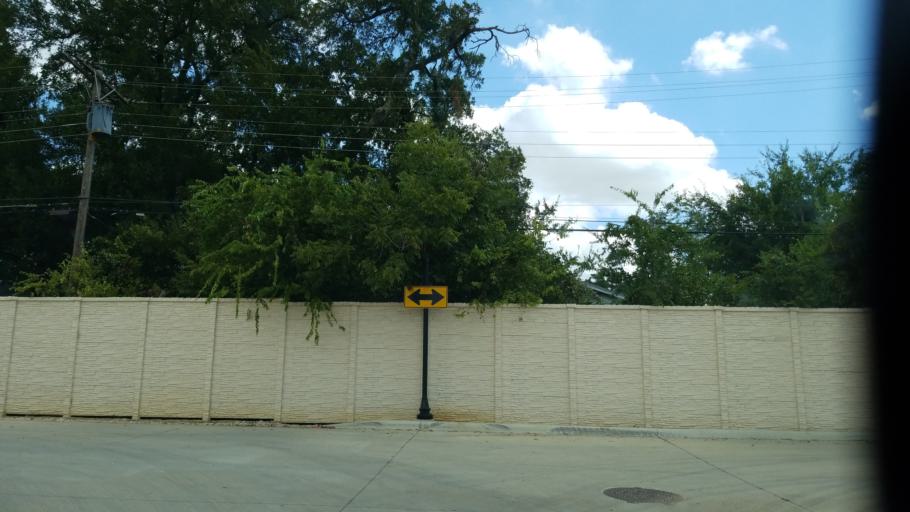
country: US
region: Texas
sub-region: Tarrant County
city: Euless
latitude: 32.8329
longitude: -97.0942
